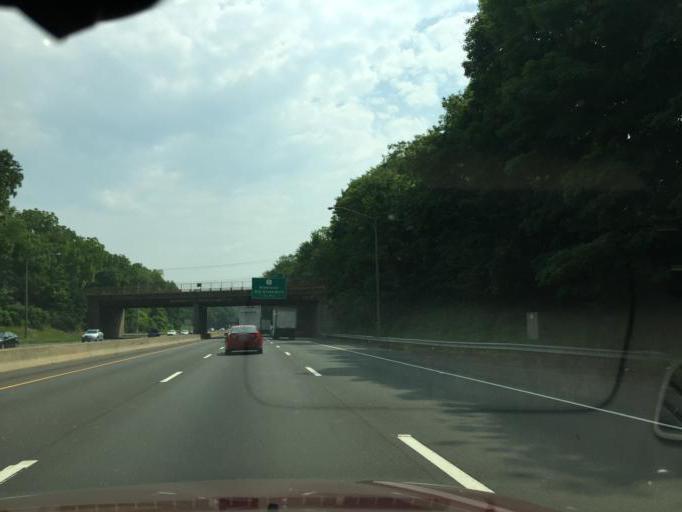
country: US
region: Connecticut
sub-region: Fairfield County
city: Riverside
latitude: 41.0380
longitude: -73.5880
